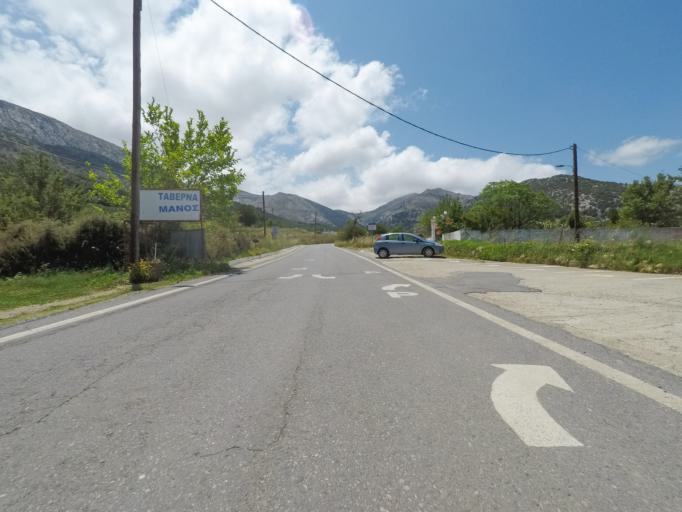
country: GR
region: Crete
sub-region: Nomos Irakleiou
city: Mokhos
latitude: 35.1701
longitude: 25.4429
